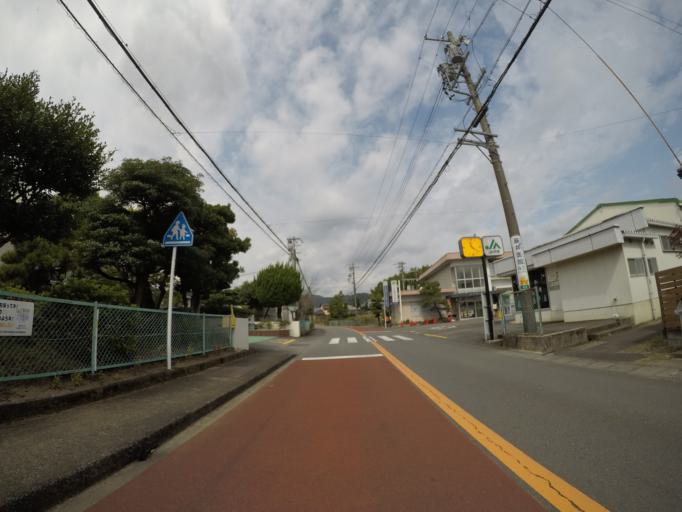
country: JP
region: Shizuoka
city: Shimada
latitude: 34.8553
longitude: 138.1813
